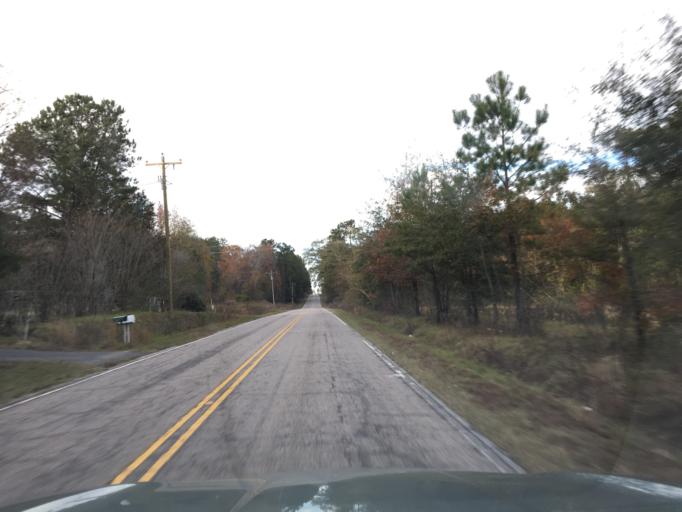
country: US
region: South Carolina
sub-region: Lexington County
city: Red Bank
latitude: 33.7416
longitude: -81.3629
